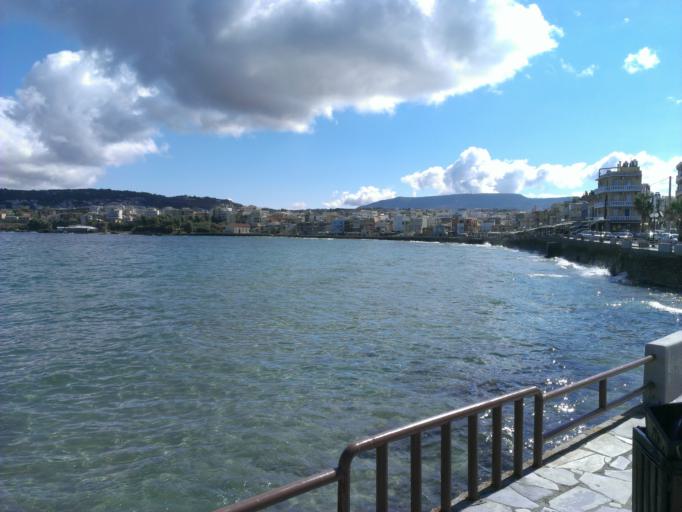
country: GR
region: Crete
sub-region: Nomos Chanias
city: Chania
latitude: 35.5181
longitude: 24.0241
